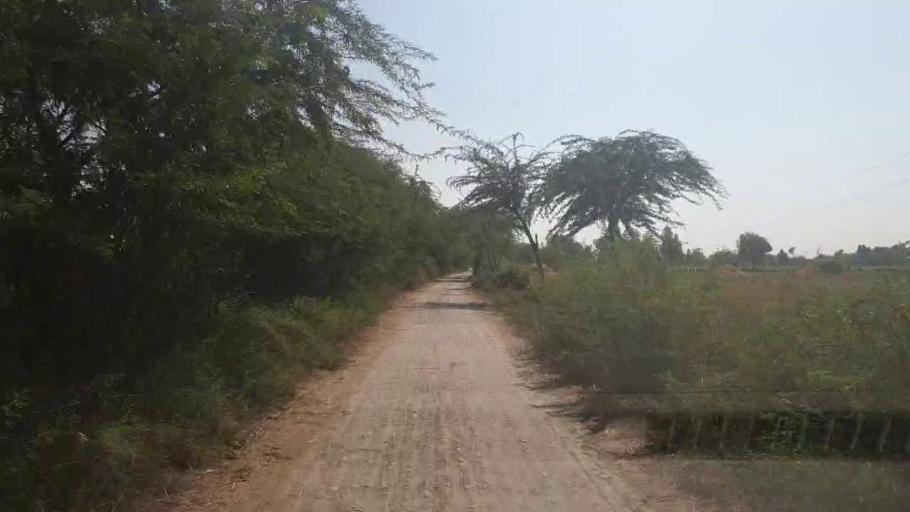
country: PK
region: Sindh
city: Badin
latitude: 24.6332
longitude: 68.9127
